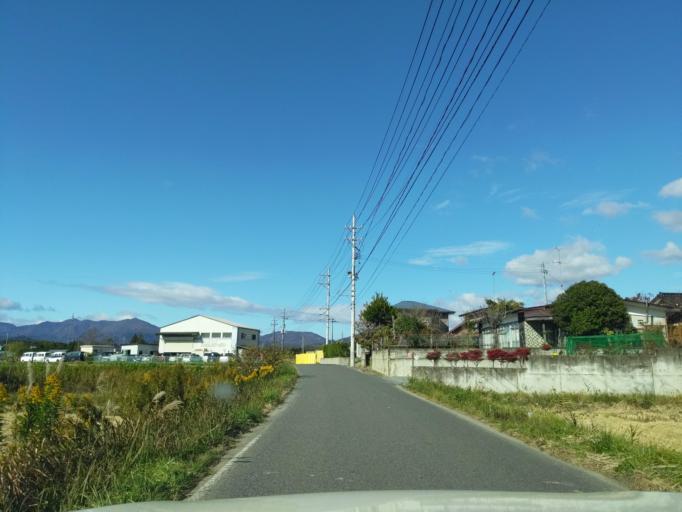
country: JP
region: Fukushima
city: Koriyama
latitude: 37.4410
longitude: 140.3332
